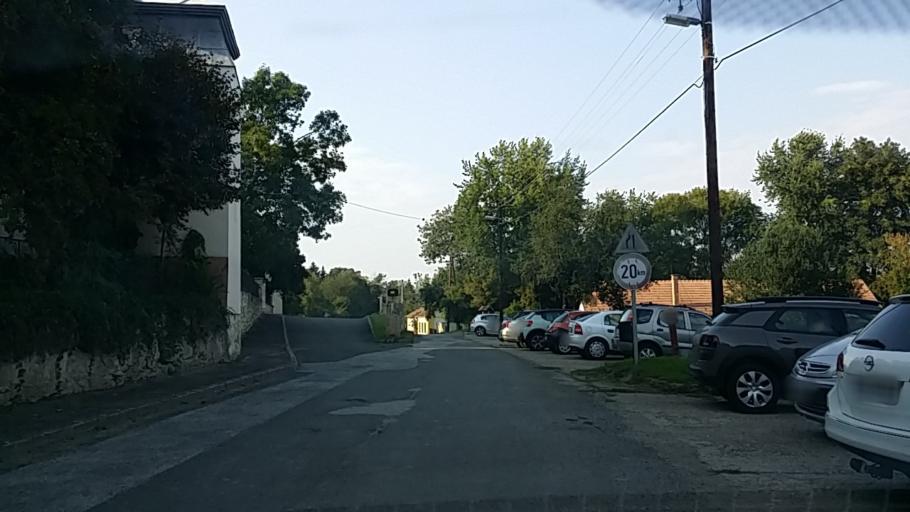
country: HU
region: Nograd
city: Bujak
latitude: 47.8240
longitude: 19.5349
